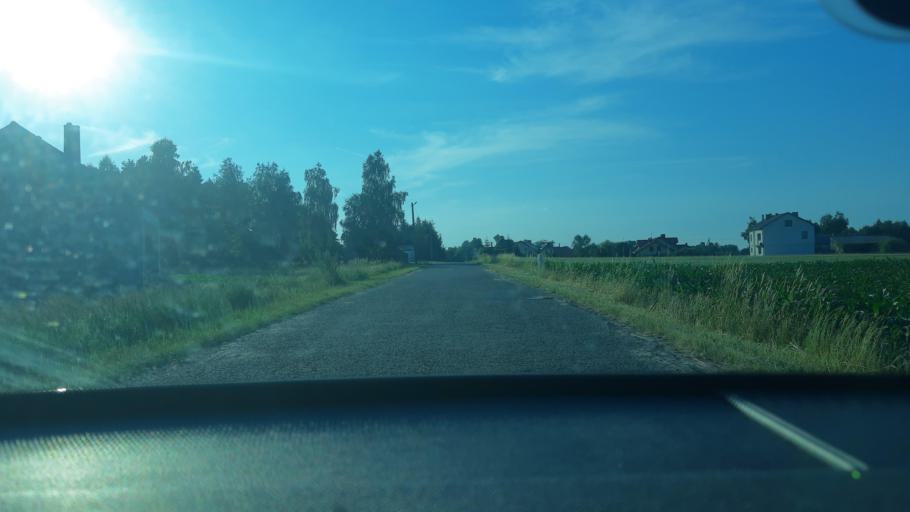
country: PL
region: Lodz Voivodeship
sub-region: Powiat sieradzki
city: Sieradz
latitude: 51.5413
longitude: 18.7587
